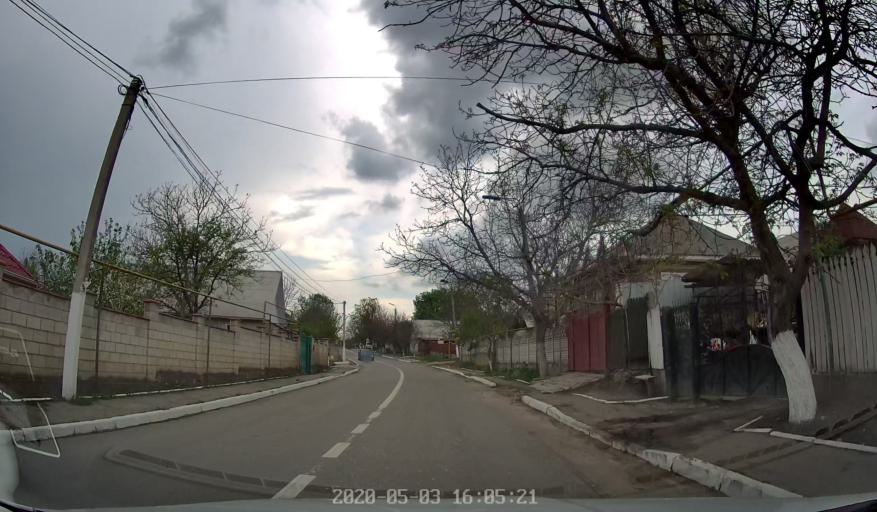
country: MD
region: Calarasi
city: Calarasi
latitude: 47.1899
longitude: 28.3579
